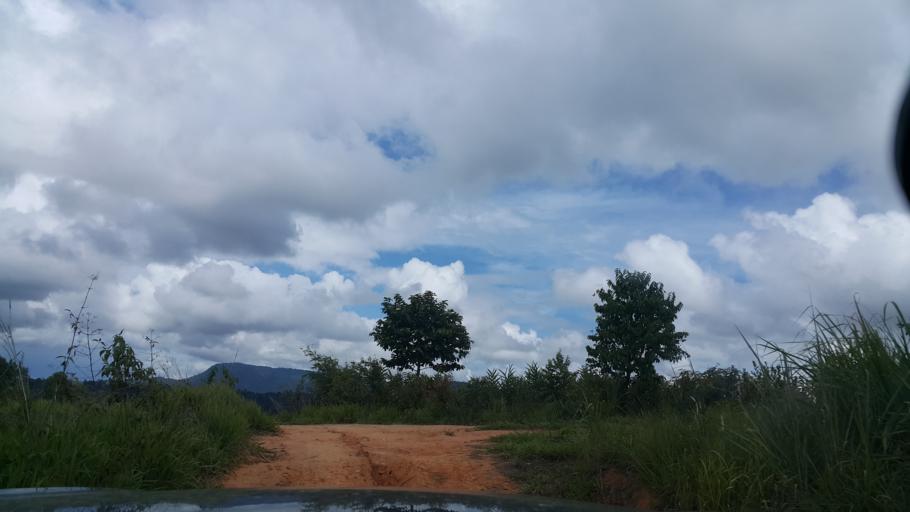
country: TH
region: Loei
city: Na Haeo
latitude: 17.5907
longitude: 100.8892
